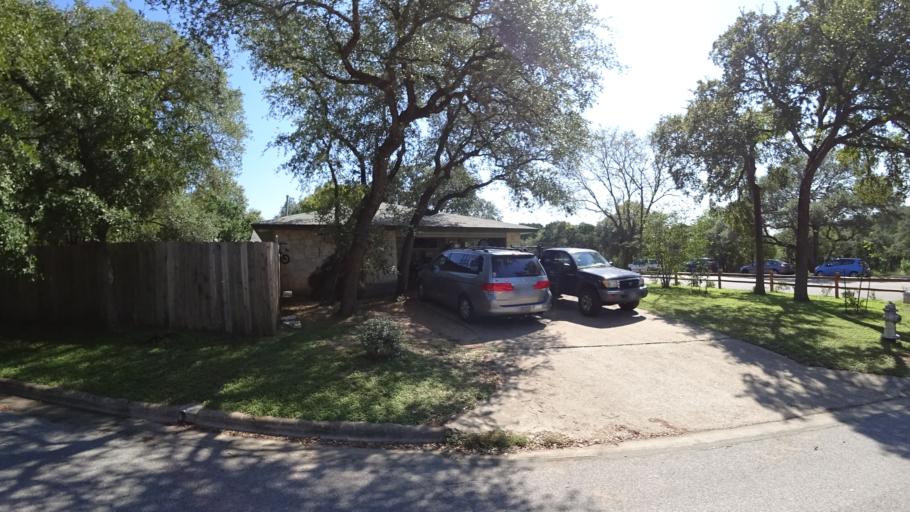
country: US
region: Texas
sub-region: Travis County
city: Rollingwood
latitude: 30.2499
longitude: -97.7951
